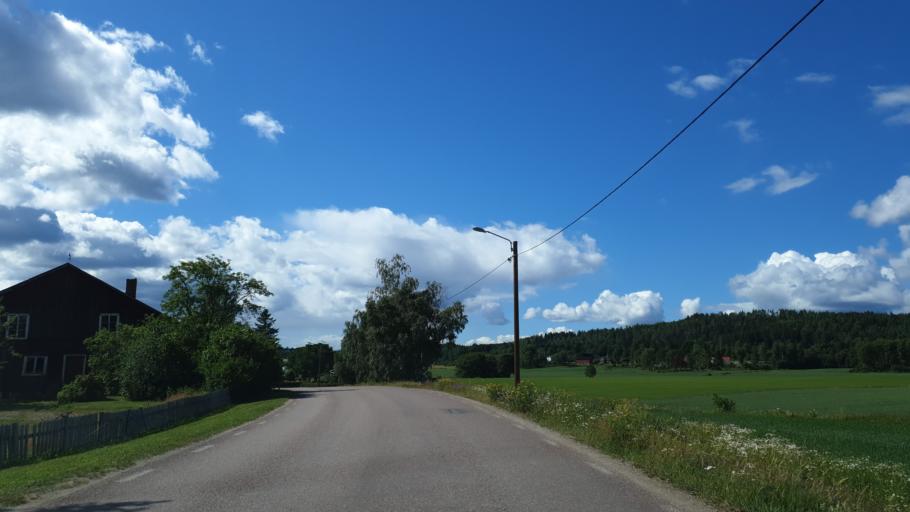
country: SE
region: Gaevleborg
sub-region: Nordanstigs Kommun
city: Bergsjoe
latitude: 62.0508
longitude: 17.2199
